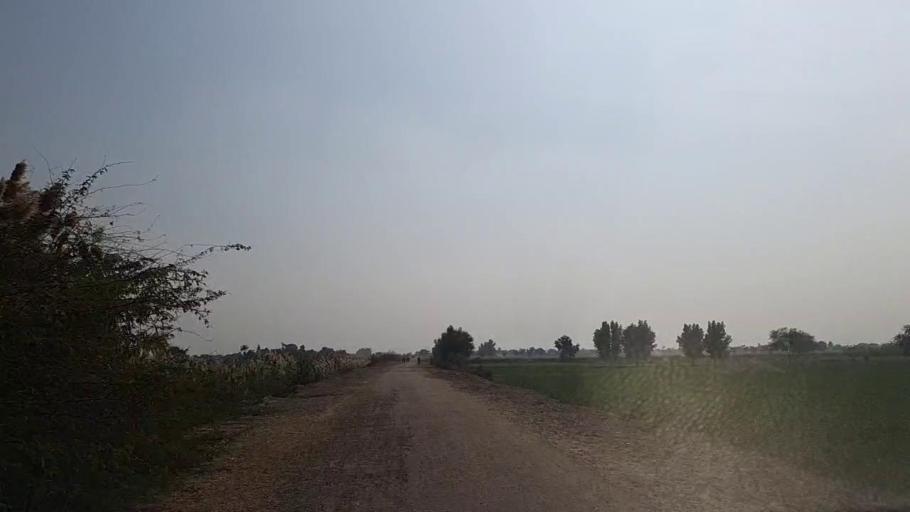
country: PK
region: Sindh
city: Daur
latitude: 26.4711
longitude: 68.4663
